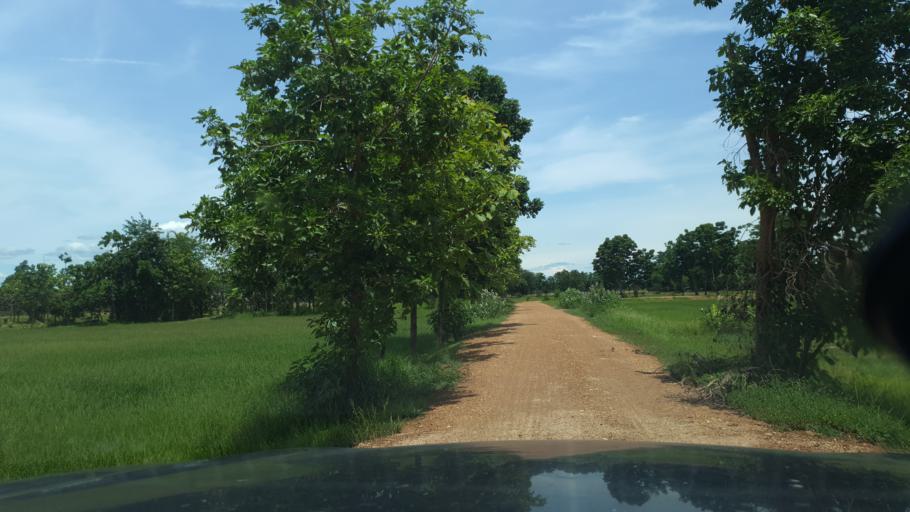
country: TH
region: Sukhothai
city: Ban Na
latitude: 17.0753
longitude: 99.6958
